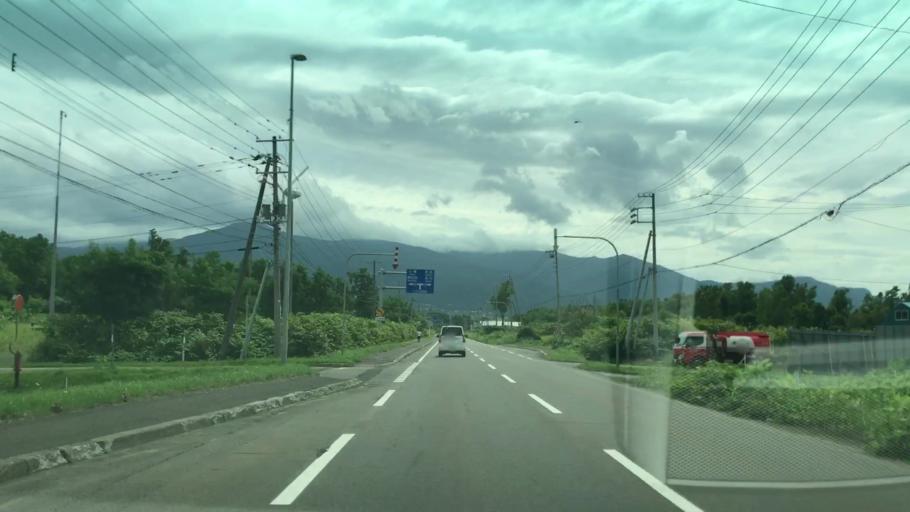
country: JP
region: Hokkaido
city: Iwanai
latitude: 43.0017
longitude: 140.5406
